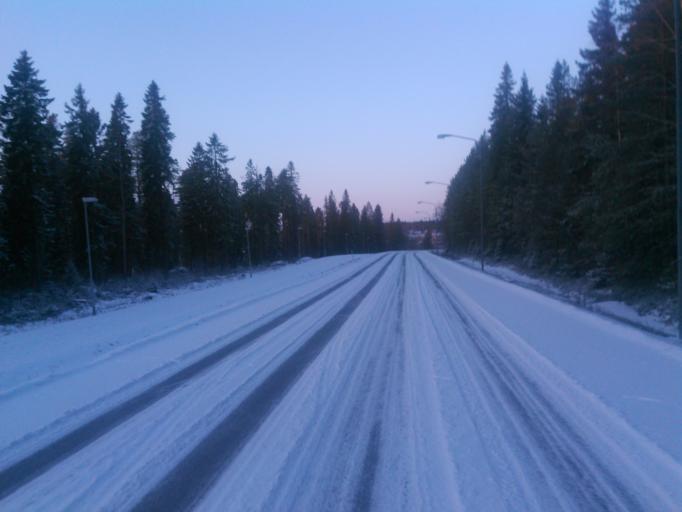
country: SE
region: Vaesterbotten
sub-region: Umea Kommun
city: Umea
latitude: 63.8223
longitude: 20.3160
